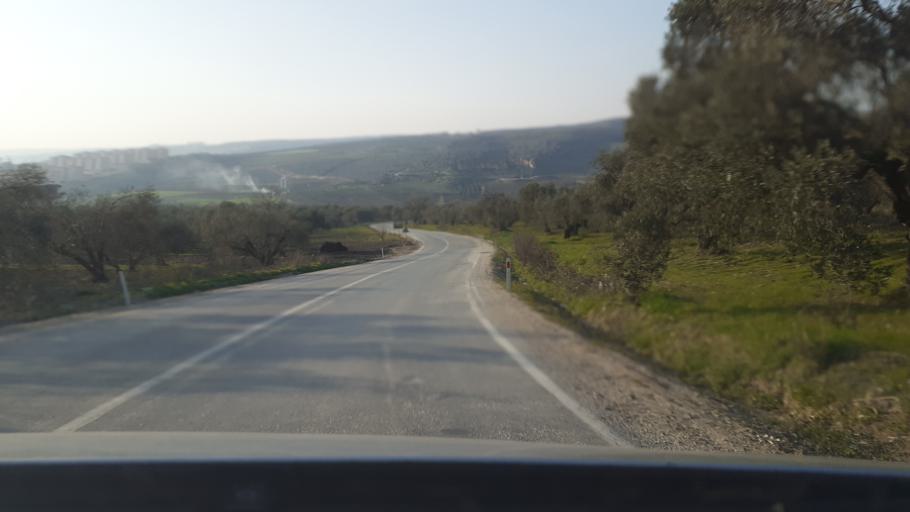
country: TR
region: Hatay
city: Oymakli
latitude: 36.1134
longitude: 36.2865
